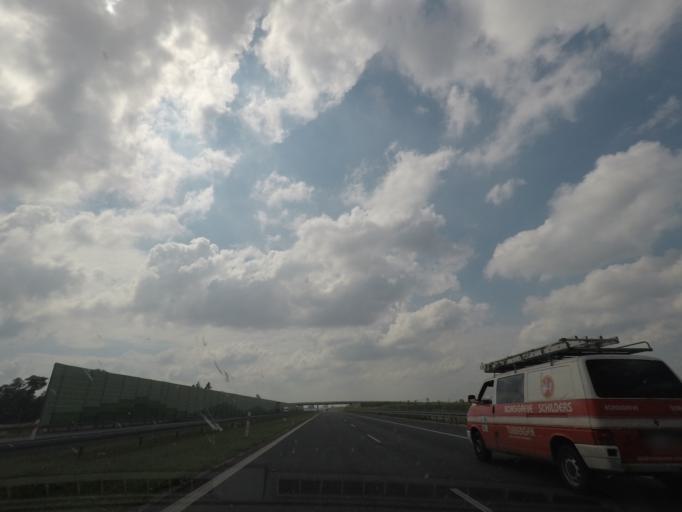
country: PL
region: Lodz Voivodeship
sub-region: Powiat kutnowski
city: Krzyzanow
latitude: 52.1597
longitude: 19.4829
